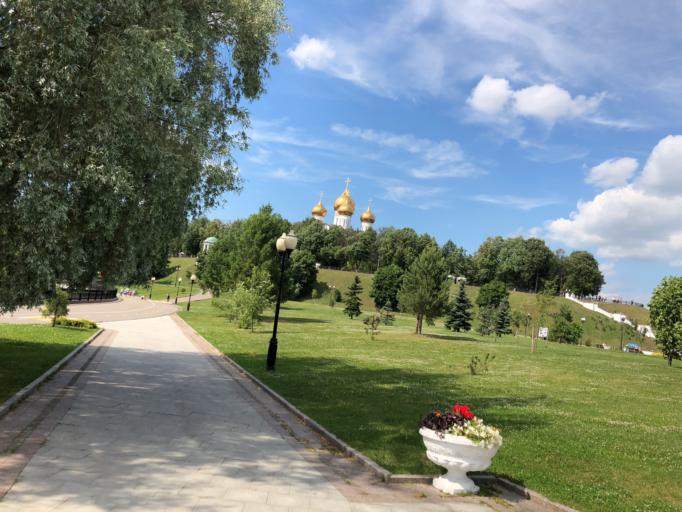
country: RU
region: Jaroslavl
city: Yaroslavl
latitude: 57.6199
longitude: 39.9037
